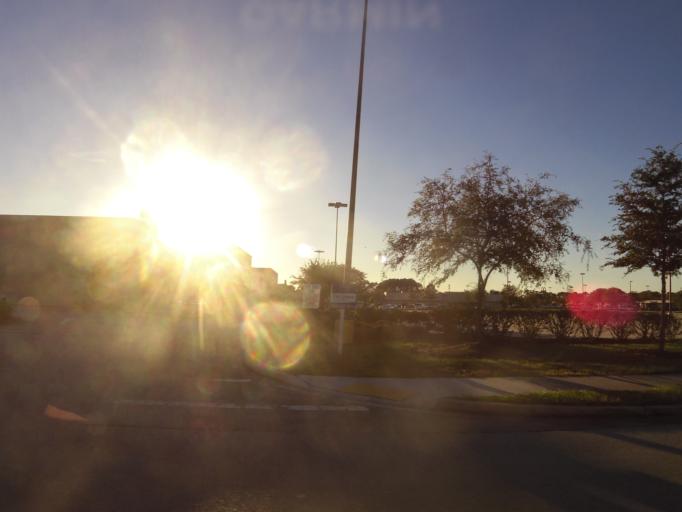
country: US
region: Florida
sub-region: Duval County
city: Jacksonville Beach
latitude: 30.2861
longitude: -81.4378
